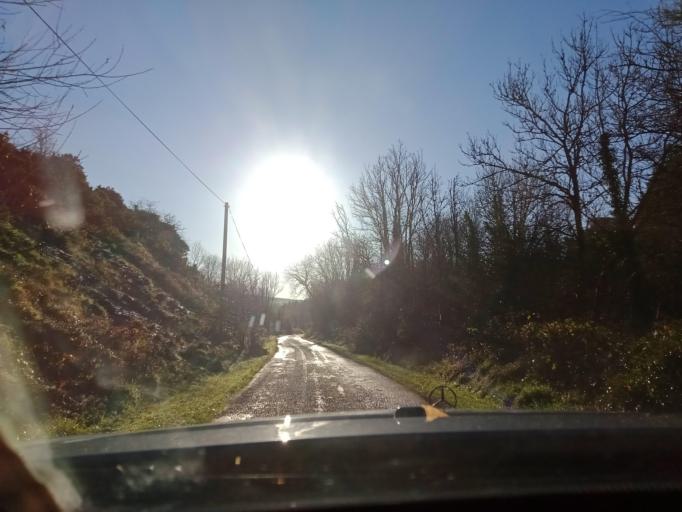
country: IE
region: Munster
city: Carrick-on-Suir
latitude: 52.4243
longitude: -7.3845
